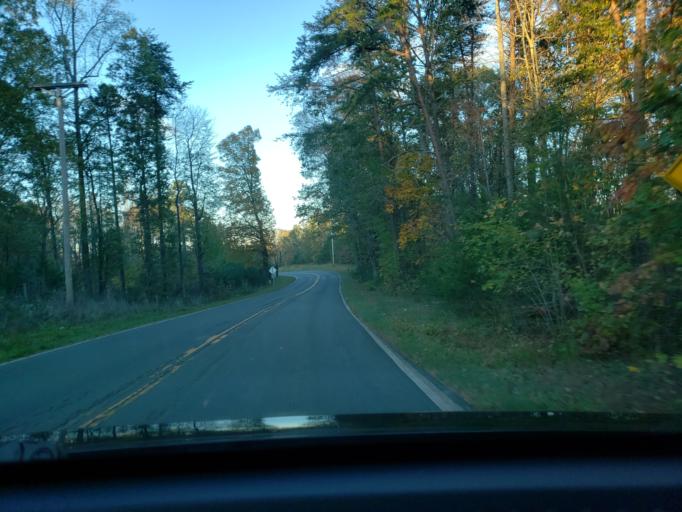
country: US
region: North Carolina
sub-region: Stokes County
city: Danbury
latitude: 36.3756
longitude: -80.1887
